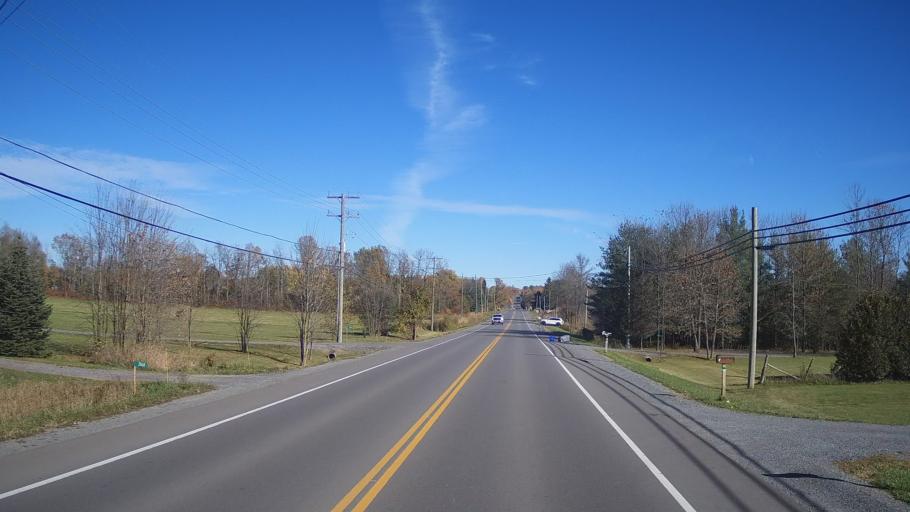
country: CA
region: Ontario
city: Kingston
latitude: 44.4064
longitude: -76.6146
